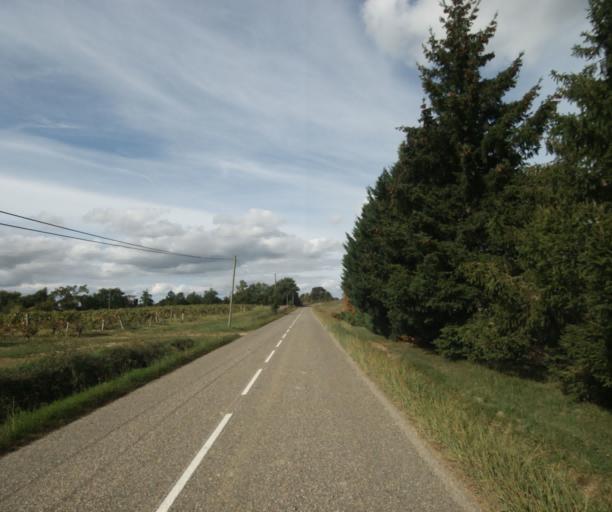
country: FR
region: Midi-Pyrenees
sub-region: Departement du Gers
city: Eauze
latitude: 43.8372
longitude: 0.1511
